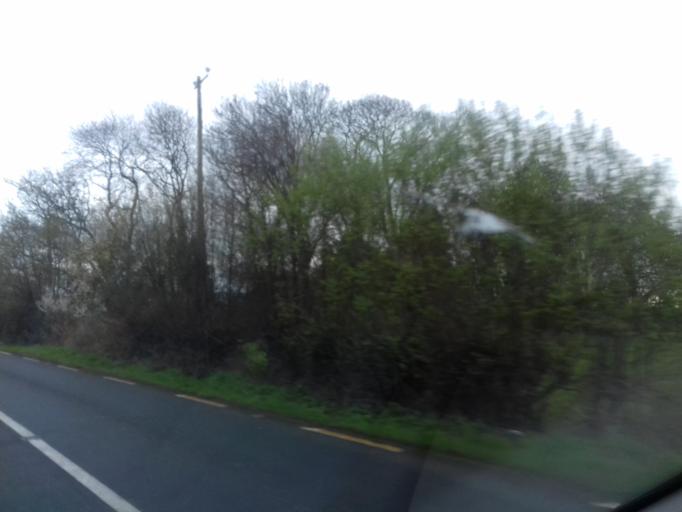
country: IE
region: Ulster
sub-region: An Cabhan
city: Ballyconnell
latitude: 54.0922
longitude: -7.5495
